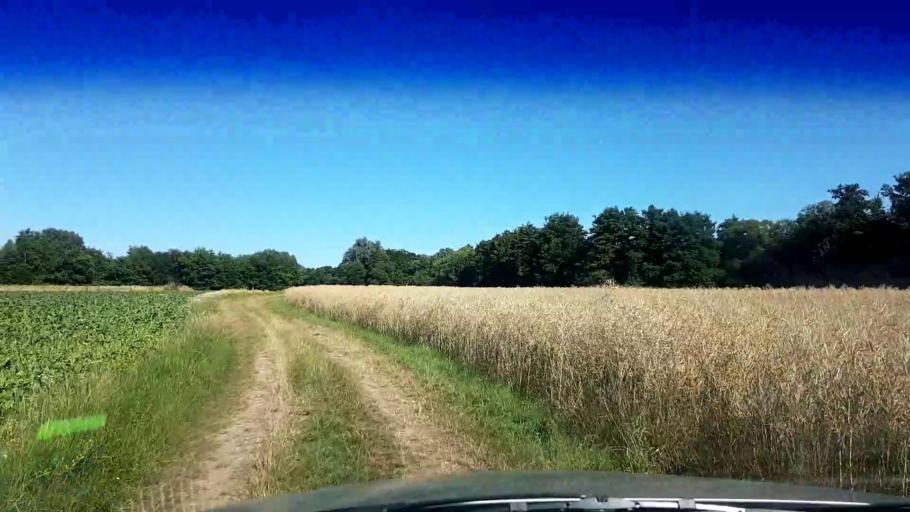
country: DE
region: Bavaria
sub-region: Upper Franconia
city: Bischberg
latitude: 49.9175
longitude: 10.8301
